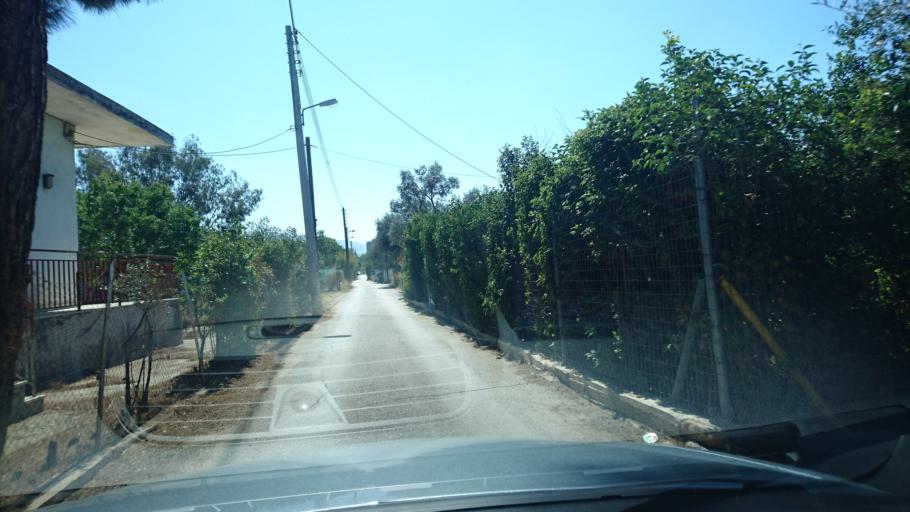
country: GR
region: Attica
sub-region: Nomarchia Athinas
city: Khalandrion
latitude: 38.0166
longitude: 23.8113
